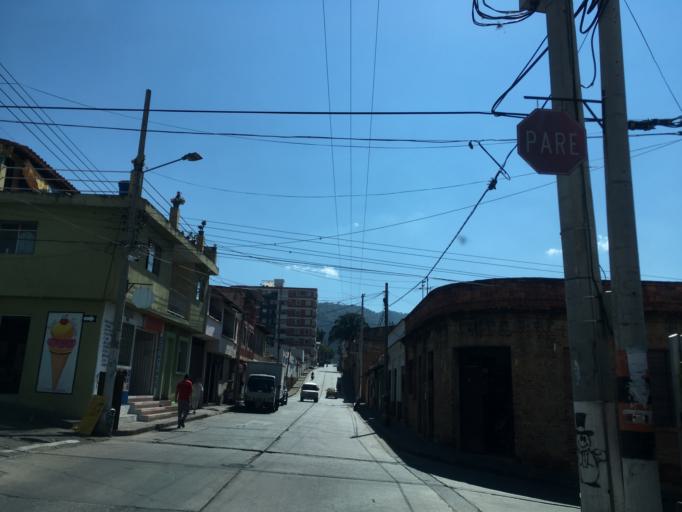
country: CO
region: Santander
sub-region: San Gil
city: San Gil
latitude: 6.5588
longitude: -73.1341
